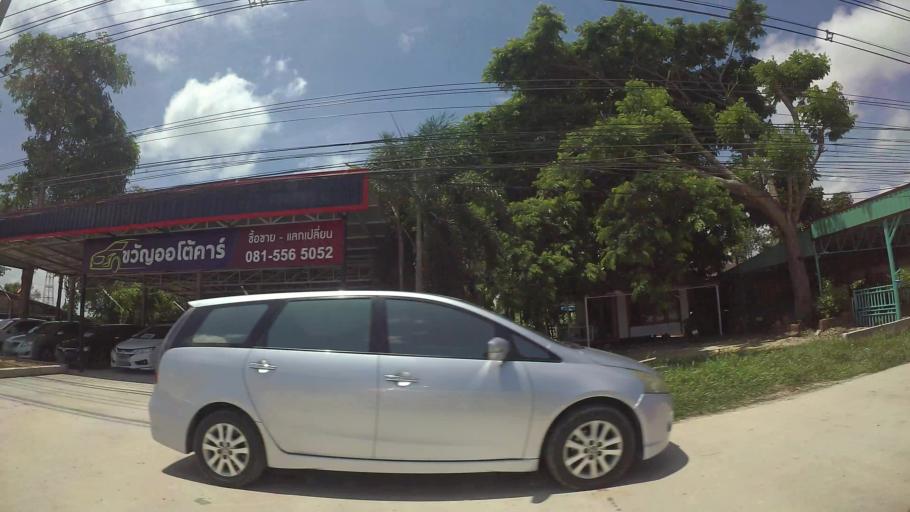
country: TH
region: Rayong
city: Rayong
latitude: 12.7071
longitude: 101.2392
